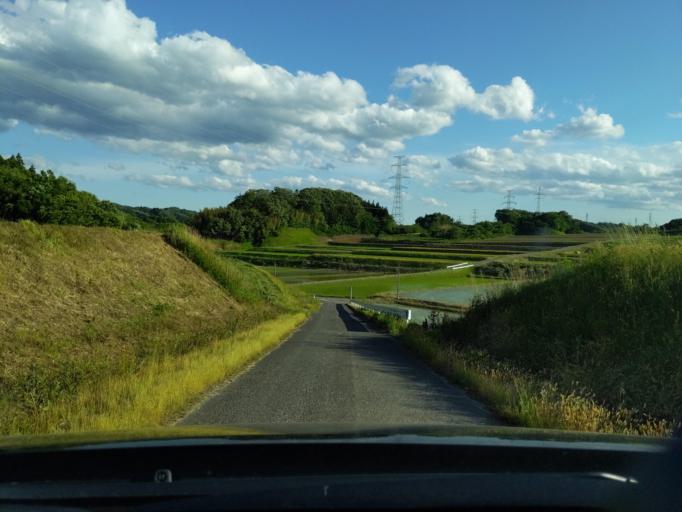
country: JP
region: Fukushima
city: Miharu
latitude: 37.4022
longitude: 140.4506
